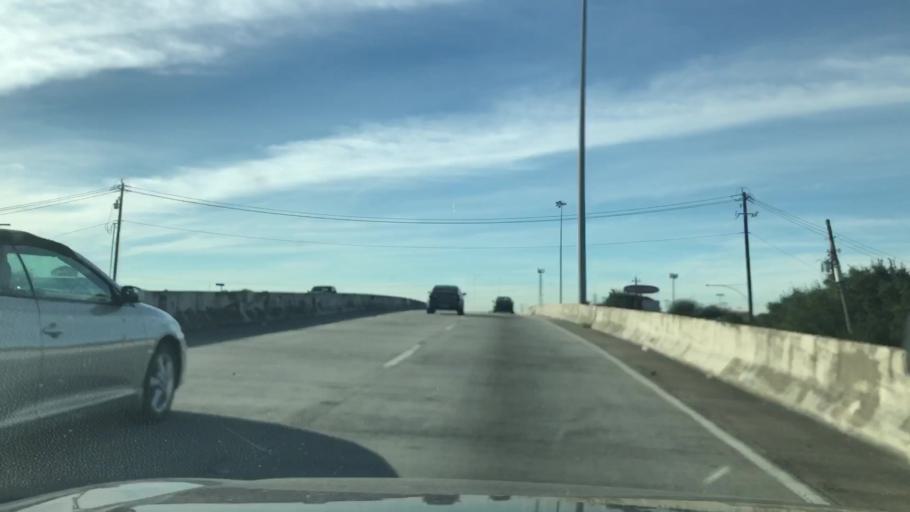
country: US
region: Texas
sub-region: Harris County
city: Bellaire
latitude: 29.6714
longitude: -95.4617
